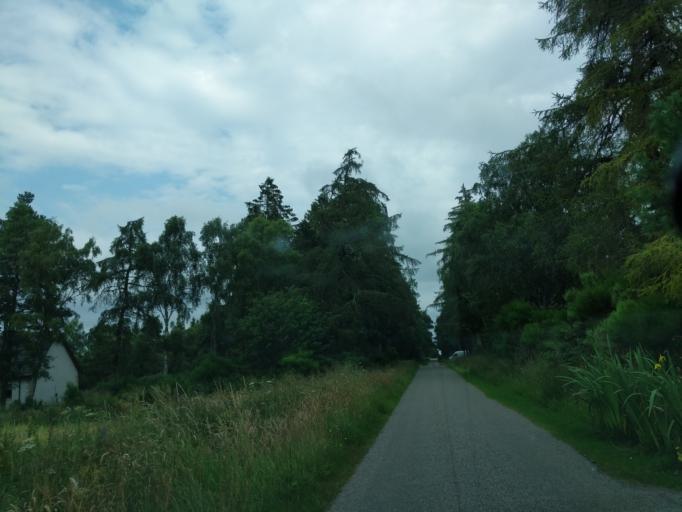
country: GB
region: Scotland
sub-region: Moray
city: Rothes
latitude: 57.4816
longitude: -3.2337
